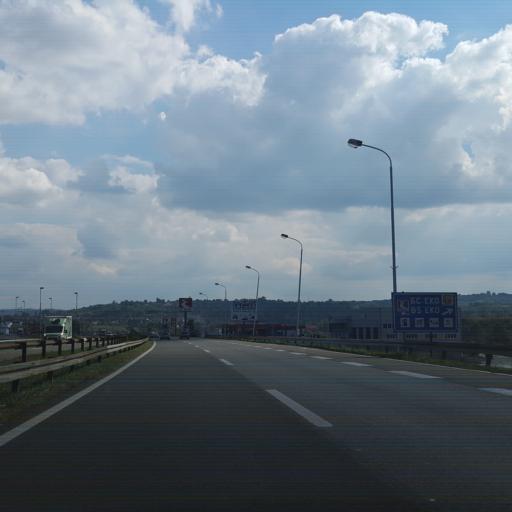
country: RS
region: Central Serbia
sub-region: Belgrade
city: Sopot
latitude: 44.5771
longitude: 20.6461
